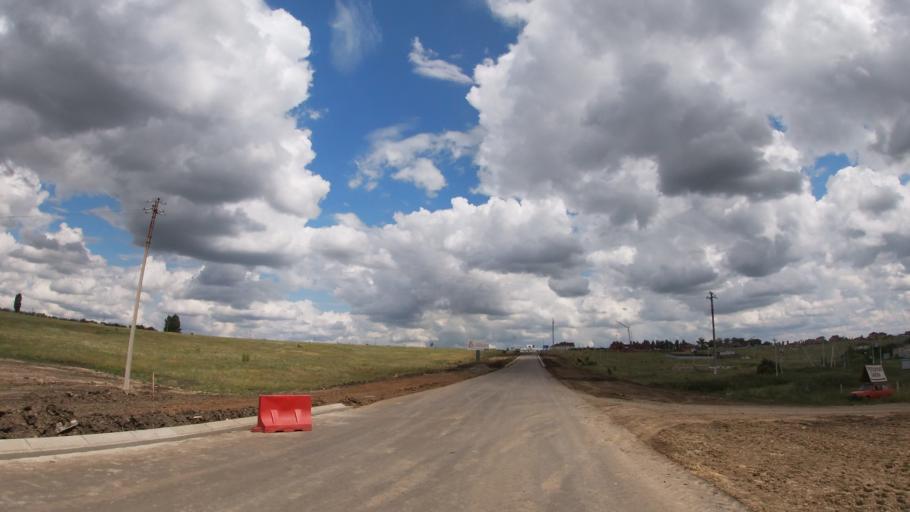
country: RU
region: Belgorod
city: Mayskiy
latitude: 50.5243
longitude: 36.5132
